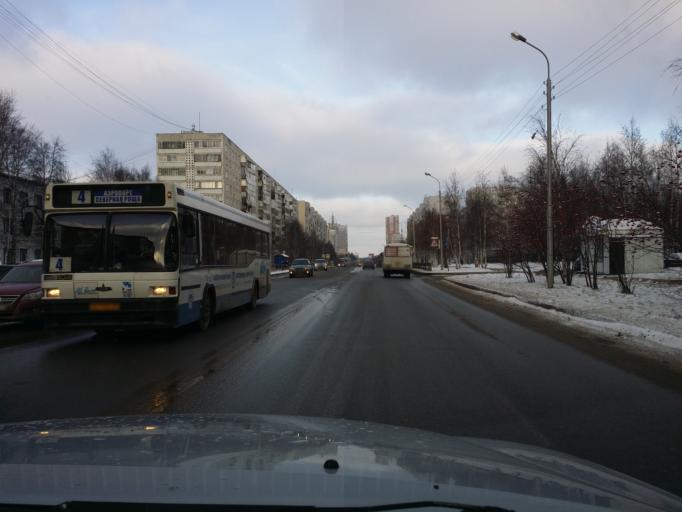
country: RU
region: Khanty-Mansiyskiy Avtonomnyy Okrug
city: Nizhnevartovsk
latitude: 60.9270
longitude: 76.5932
